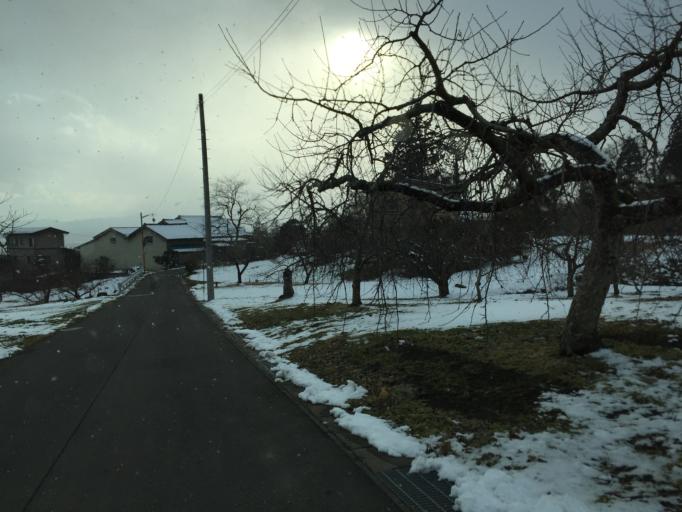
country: JP
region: Fukushima
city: Hobaramachi
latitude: 37.8432
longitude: 140.4654
